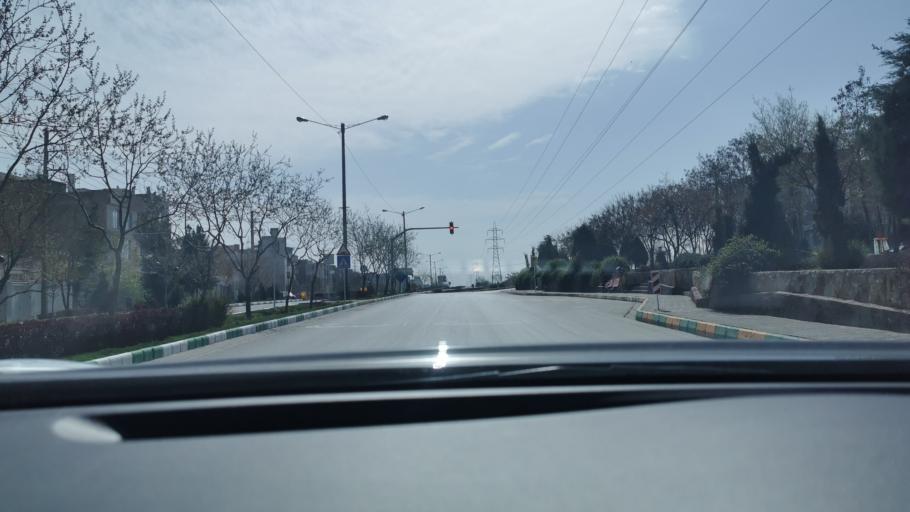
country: IR
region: Razavi Khorasan
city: Mashhad
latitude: 36.2888
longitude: 59.5332
